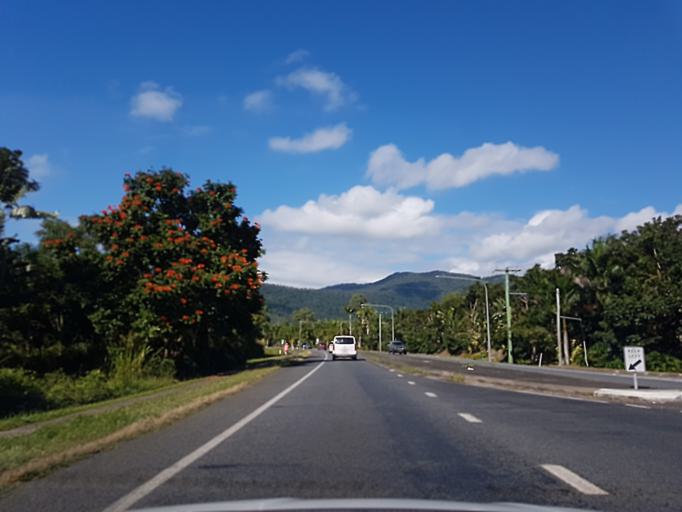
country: AU
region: Queensland
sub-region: Cairns
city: Trinity Beach
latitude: -16.7826
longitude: 145.6734
